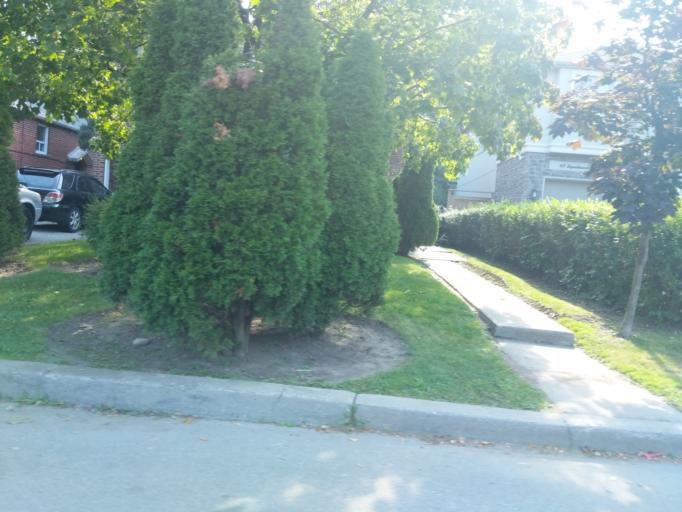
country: CA
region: Ontario
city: Toronto
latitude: 43.7234
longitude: -79.4399
